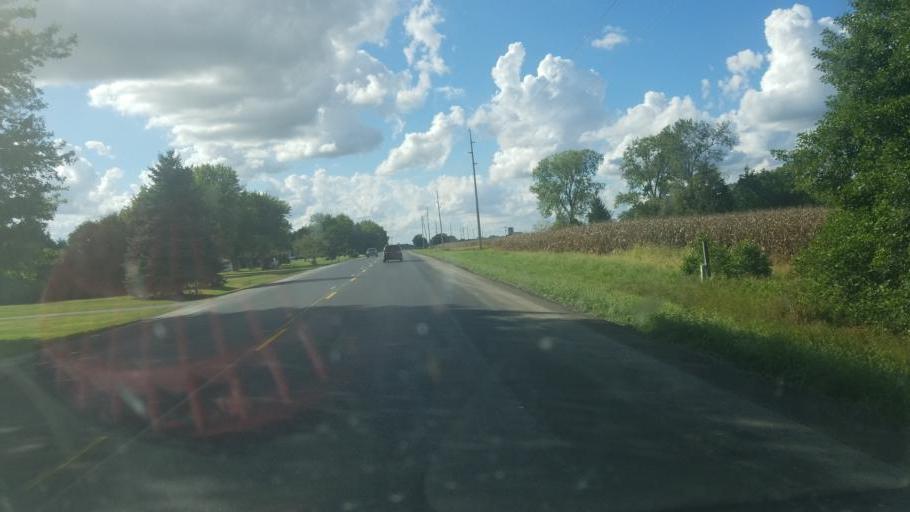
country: US
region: Ohio
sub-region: Hardin County
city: Kenton
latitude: 40.6581
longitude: -83.6396
